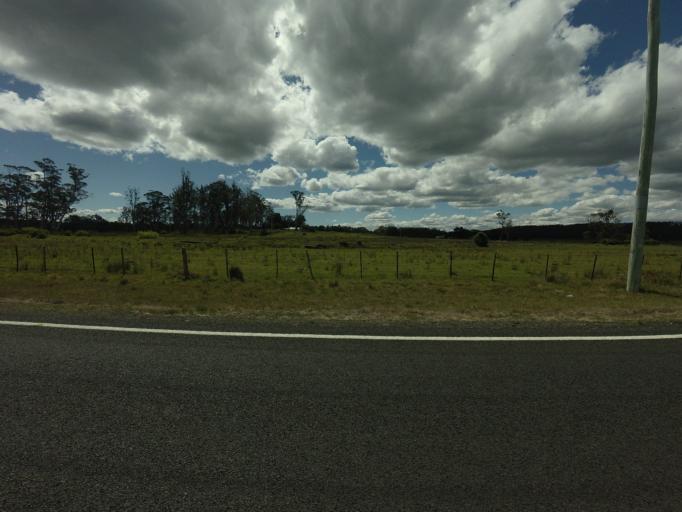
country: AU
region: Tasmania
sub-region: Northern Midlands
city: Evandale
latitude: -41.9908
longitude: 147.6824
